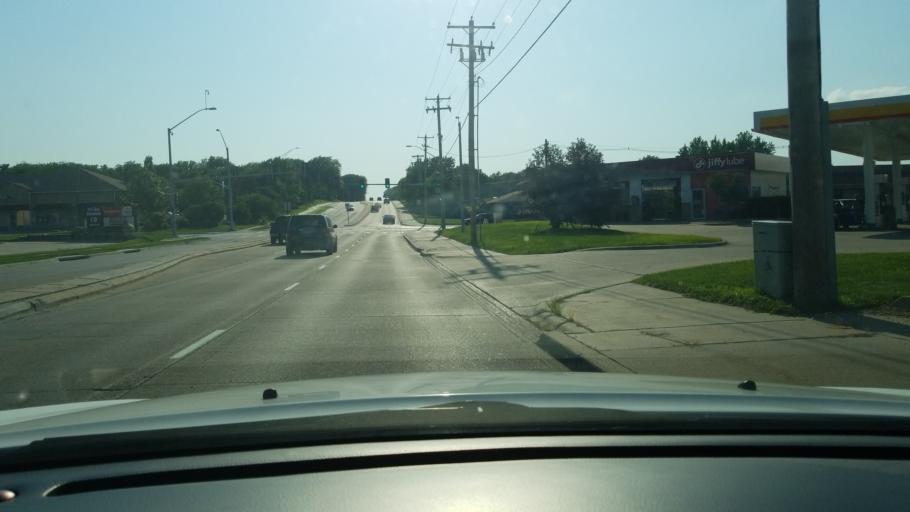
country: US
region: Nebraska
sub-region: Lancaster County
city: Lincoln
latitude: 40.7553
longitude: -96.6528
